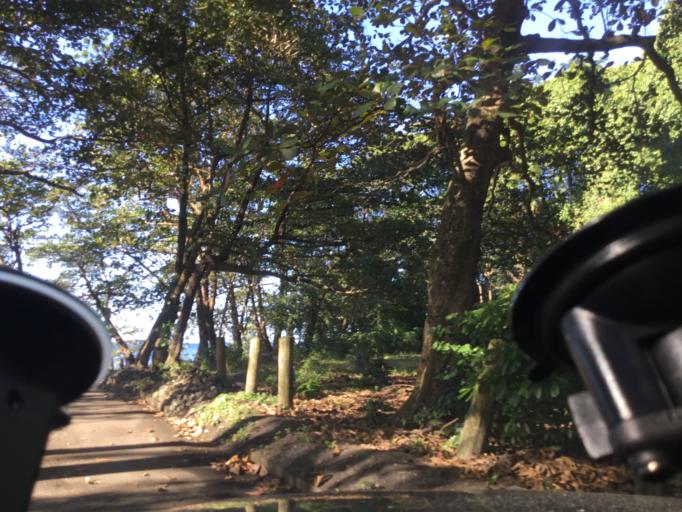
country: VC
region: Saint David
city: Chateaubelair
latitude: 13.3107
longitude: -61.2345
